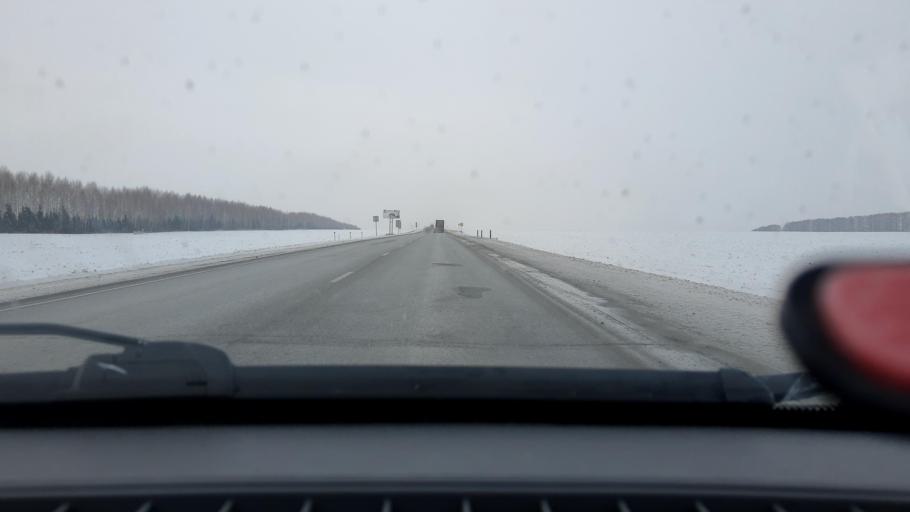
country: RU
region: Bashkortostan
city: Iglino
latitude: 54.7591
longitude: 56.3836
